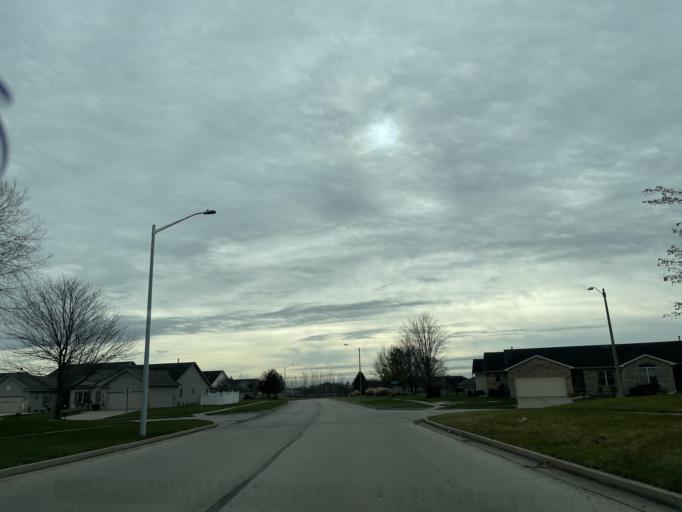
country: US
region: Illinois
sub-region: Sangamon County
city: Jerome
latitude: 39.7620
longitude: -89.7296
